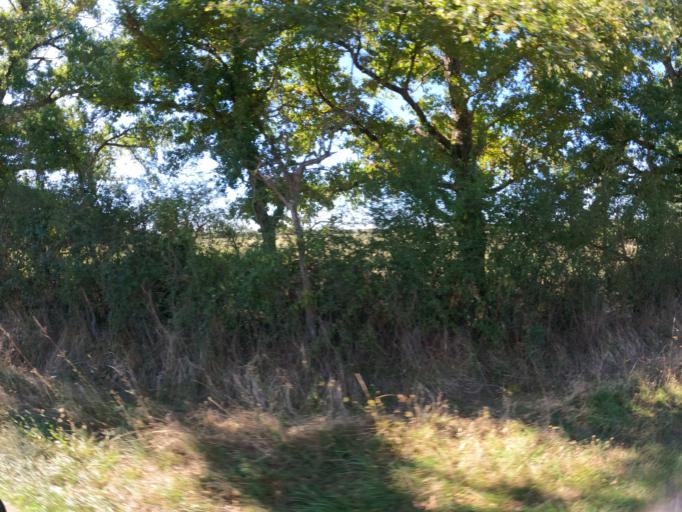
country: FR
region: Poitou-Charentes
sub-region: Departement de la Vienne
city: Lathus-Saint-Remy
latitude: 46.3151
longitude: 0.9767
